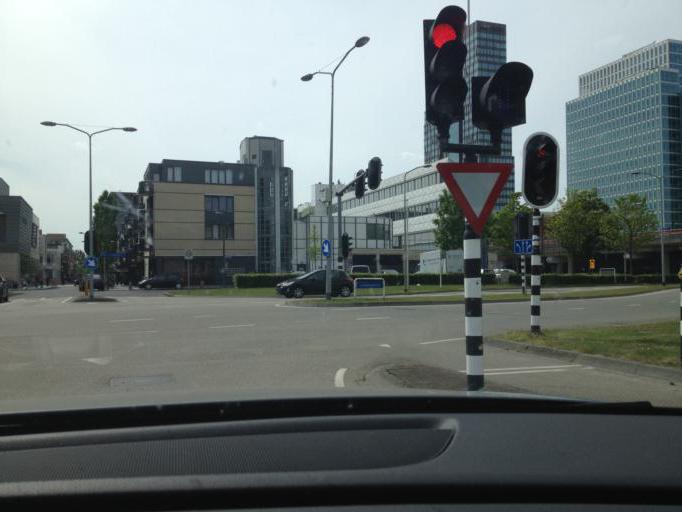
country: NL
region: Flevoland
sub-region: Gemeente Almere
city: Almere Stad
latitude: 52.3748
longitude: 5.2216
